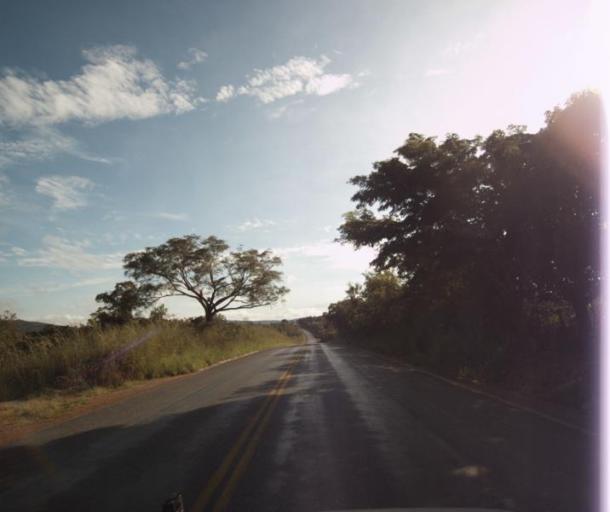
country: BR
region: Goias
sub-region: Pirenopolis
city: Pirenopolis
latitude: -15.5743
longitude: -48.6240
